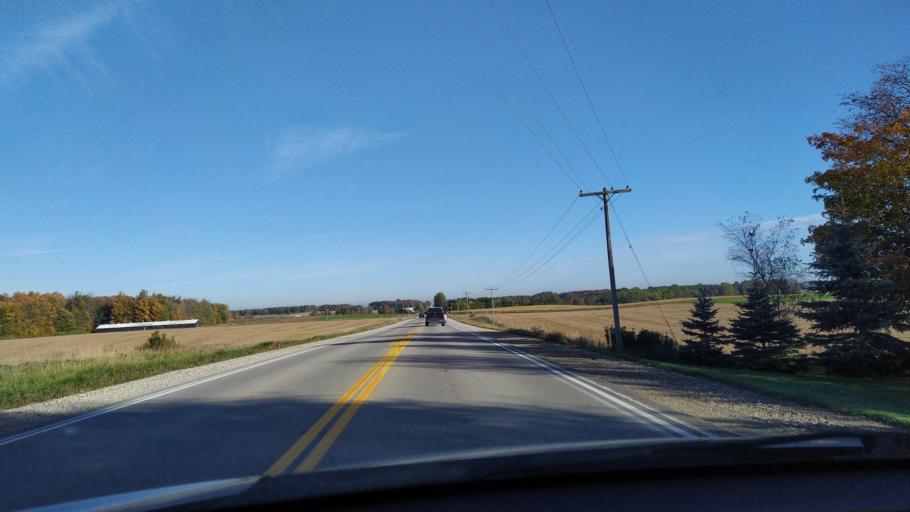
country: CA
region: Ontario
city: Stratford
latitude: 43.4487
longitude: -80.8387
